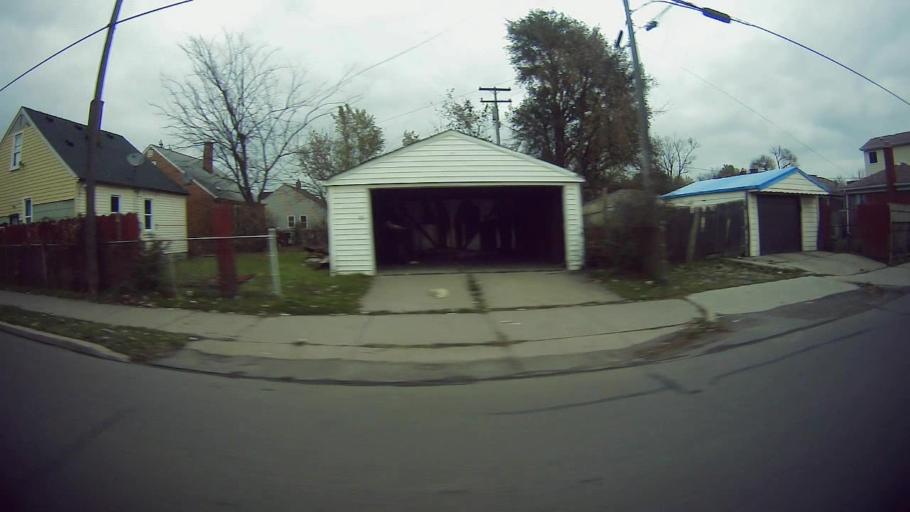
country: US
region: Michigan
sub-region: Macomb County
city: Eastpointe
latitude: 42.4411
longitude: -82.9853
